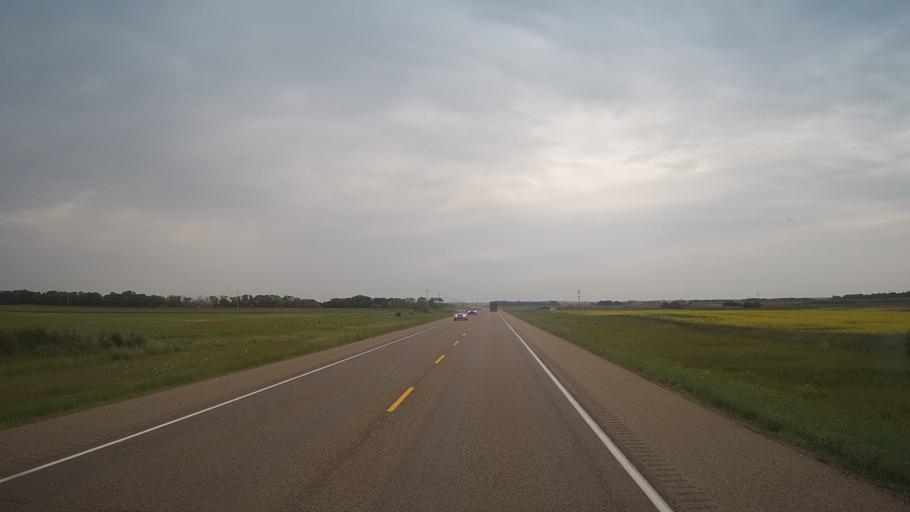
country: CA
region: Saskatchewan
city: Langham
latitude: 52.1294
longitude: -107.0925
